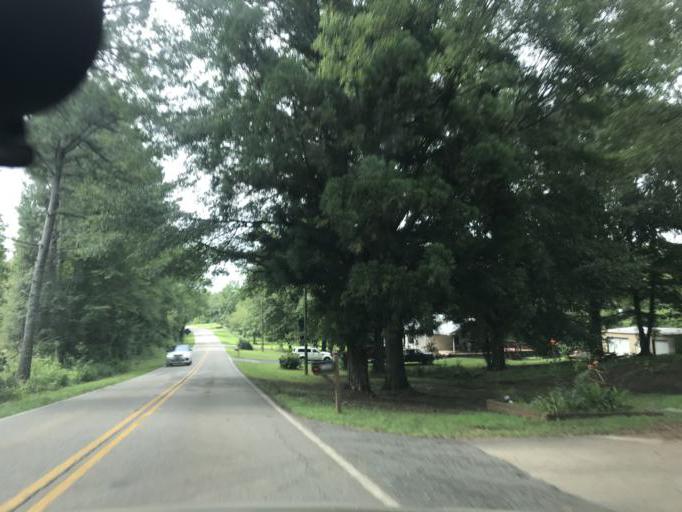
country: US
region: Georgia
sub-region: Forsyth County
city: Cumming
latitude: 34.2835
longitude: -84.2364
